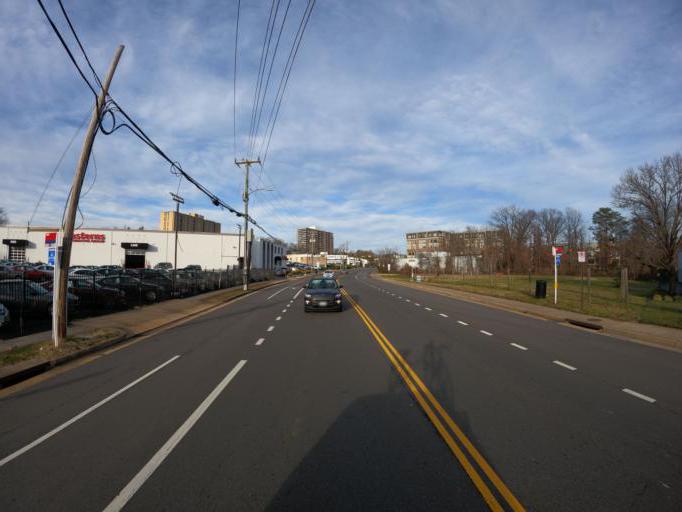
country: US
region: Virginia
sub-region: Fairfax County
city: Lincolnia
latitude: 38.8058
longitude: -77.1303
